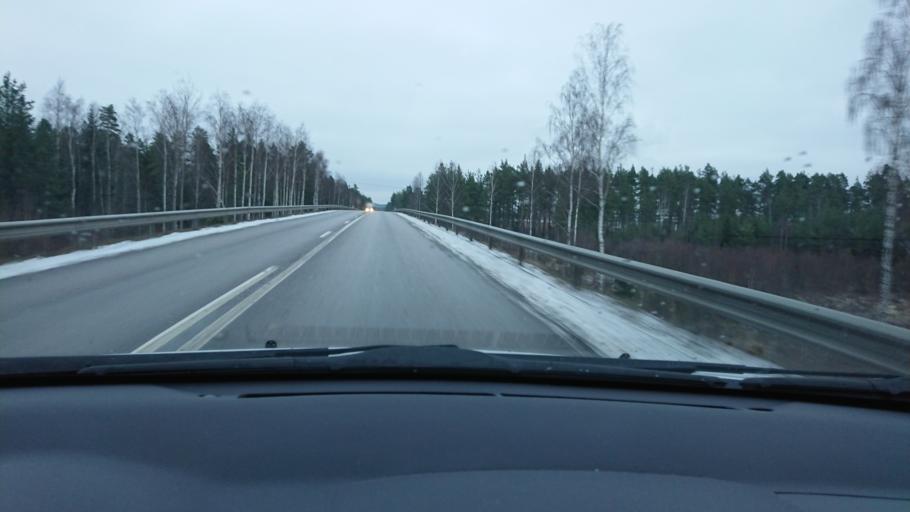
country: SE
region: Kalmar
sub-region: Hultsfreds Kommun
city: Hultsfred
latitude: 57.5035
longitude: 15.8254
